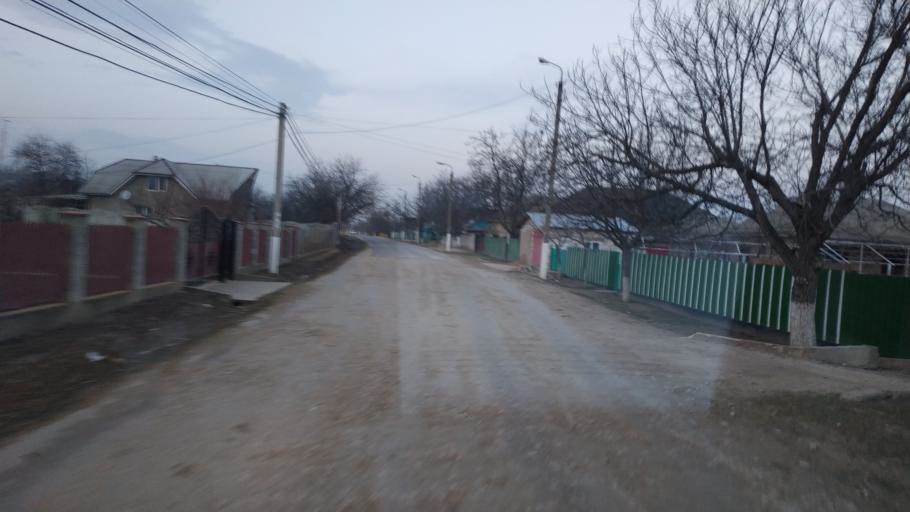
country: RO
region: Vaslui
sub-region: Comuna Stanilesti
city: Stanilesti
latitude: 46.6551
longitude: 28.3056
